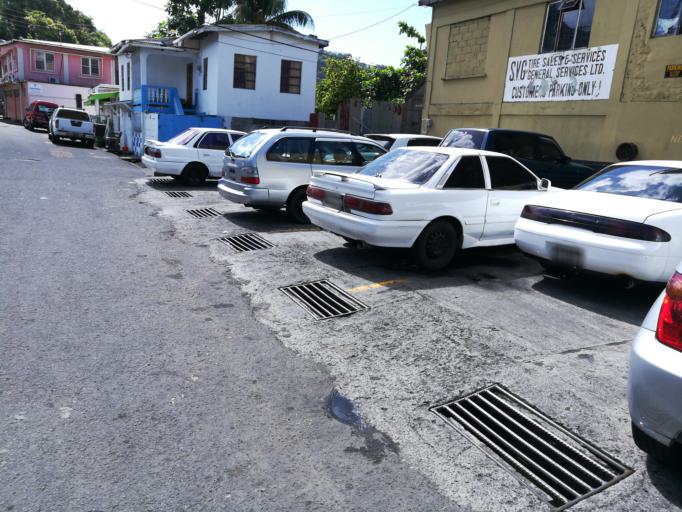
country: VC
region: Saint George
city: Kingstown
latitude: 13.1567
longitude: -61.2259
